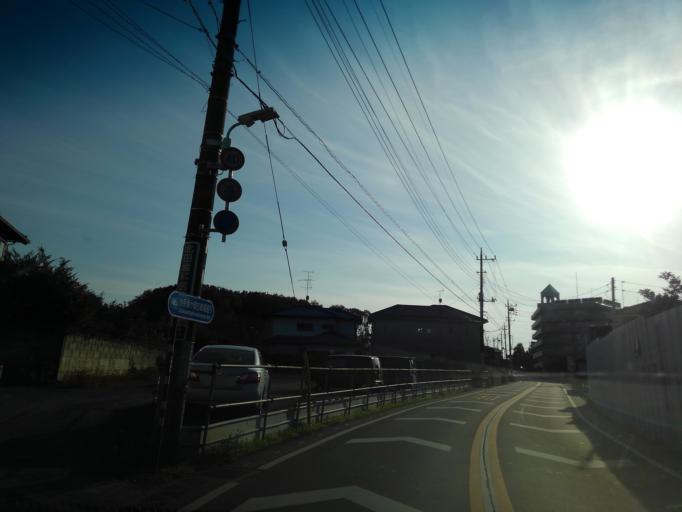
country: JP
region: Saitama
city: Tokorozawa
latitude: 35.7984
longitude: 139.4214
